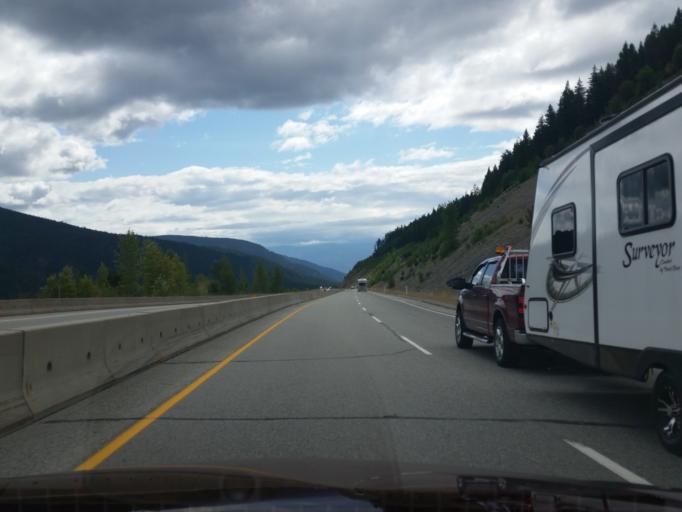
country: CA
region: British Columbia
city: Peachland
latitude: 49.8628
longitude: -119.8588
